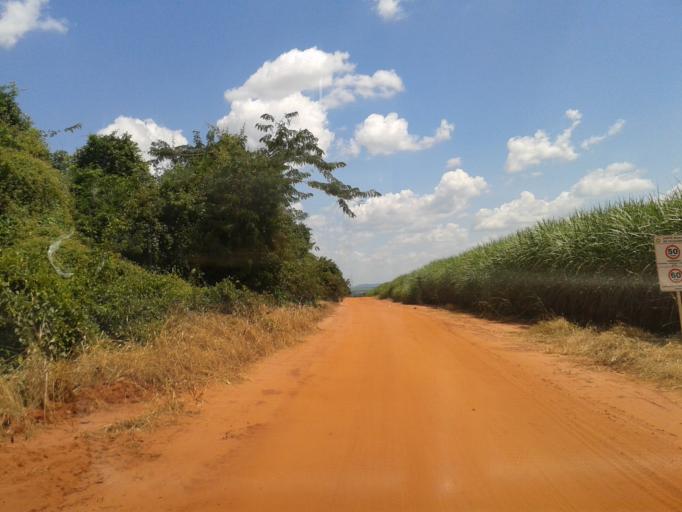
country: BR
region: Minas Gerais
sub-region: Ituiutaba
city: Ituiutaba
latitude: -19.0115
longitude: -49.6790
